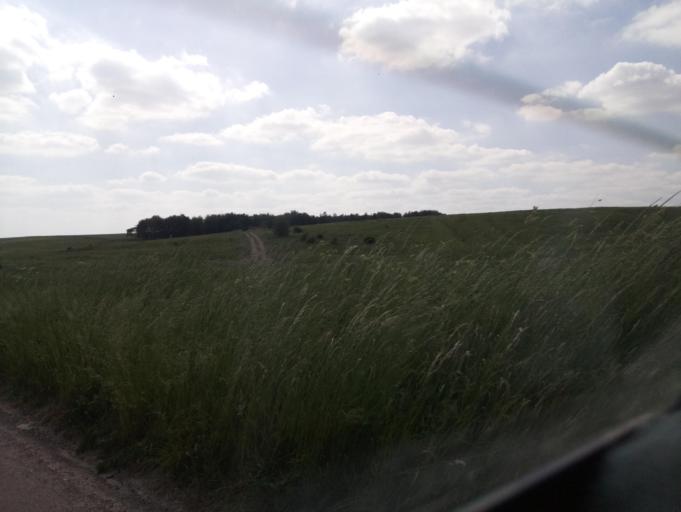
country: GB
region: England
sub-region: Wiltshire
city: Tidworth
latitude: 51.2665
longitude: -1.7222
